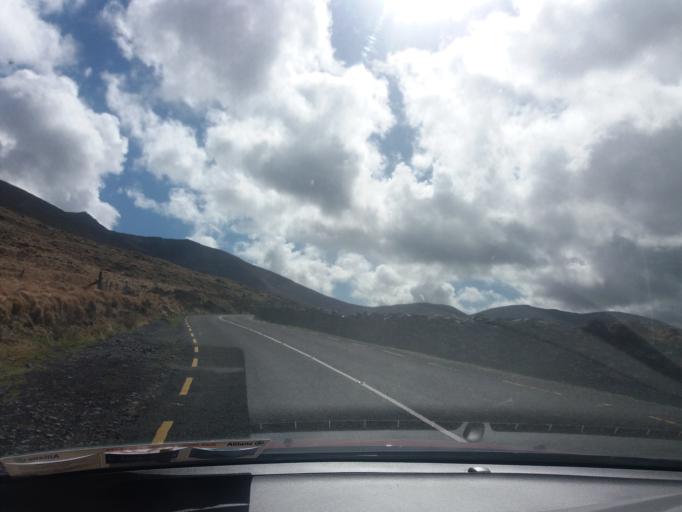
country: IE
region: Munster
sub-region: Ciarrai
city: Dingle
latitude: 52.2040
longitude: -10.1744
